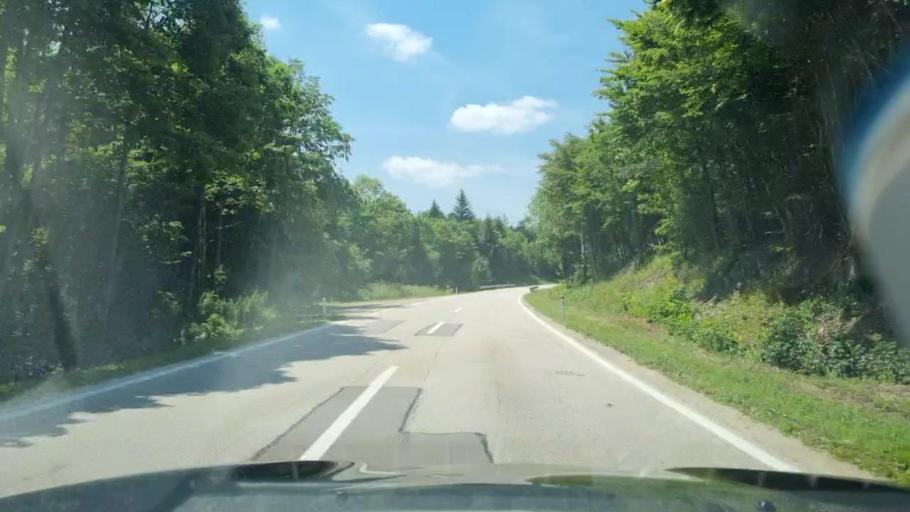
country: BA
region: Federation of Bosnia and Herzegovina
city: Sanica
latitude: 44.5509
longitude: 16.6458
